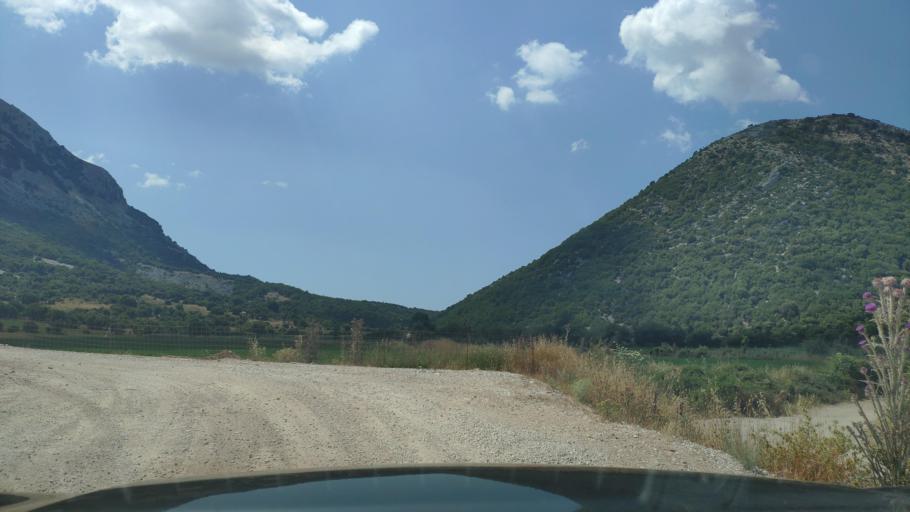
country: GR
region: West Greece
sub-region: Nomos Aitolias kai Akarnanias
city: Kandila
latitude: 38.7765
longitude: 20.9726
